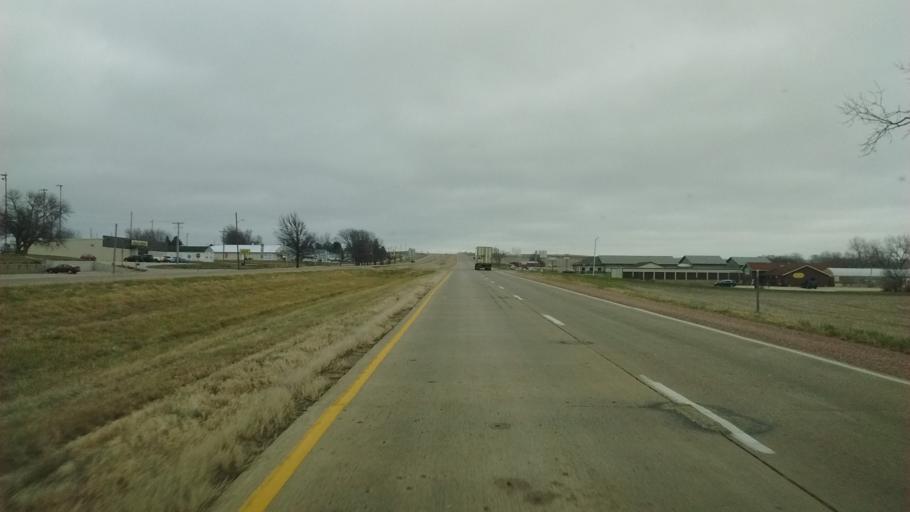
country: US
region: Iowa
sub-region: Woodbury County
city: Moville
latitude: 42.4817
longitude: -96.0671
